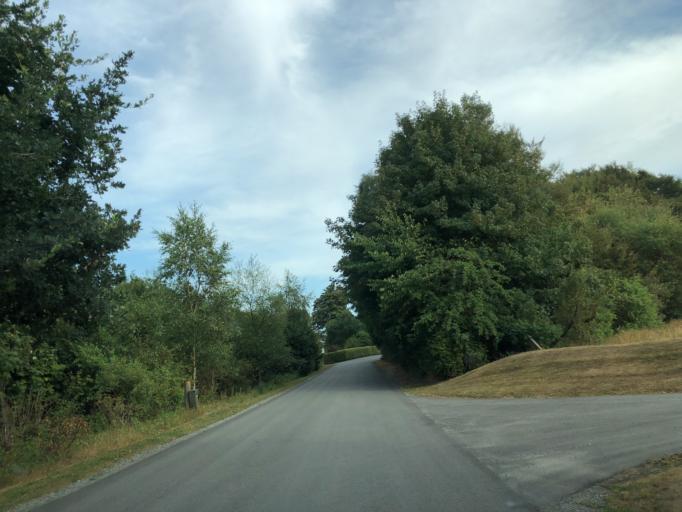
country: DK
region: South Denmark
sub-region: Vejle Kommune
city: Egtved
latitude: 55.6808
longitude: 9.2676
